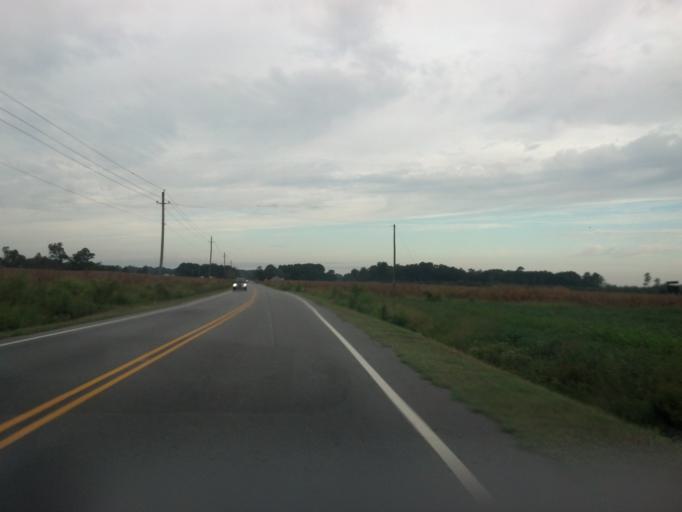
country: US
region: North Carolina
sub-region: Pitt County
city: Ayden
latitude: 35.4767
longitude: -77.4479
